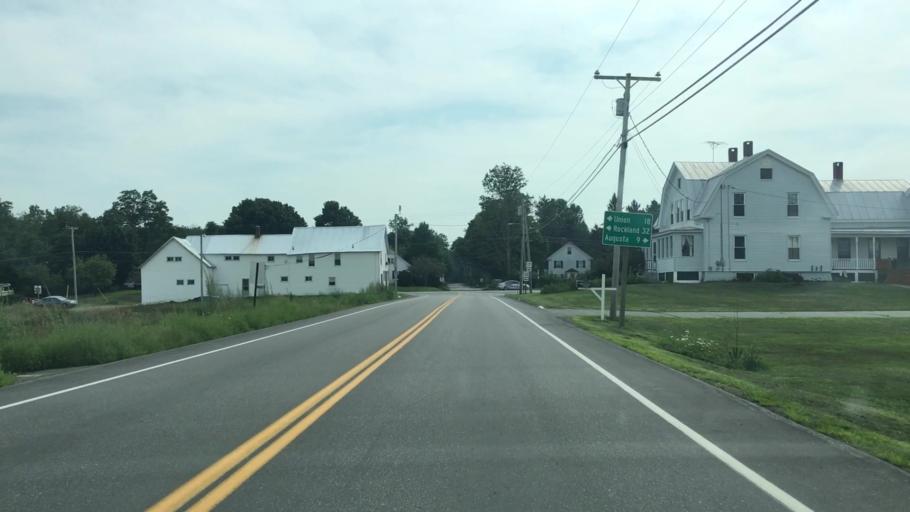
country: US
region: Maine
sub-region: Kennebec County
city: Windsor
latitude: 44.2801
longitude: -69.5978
